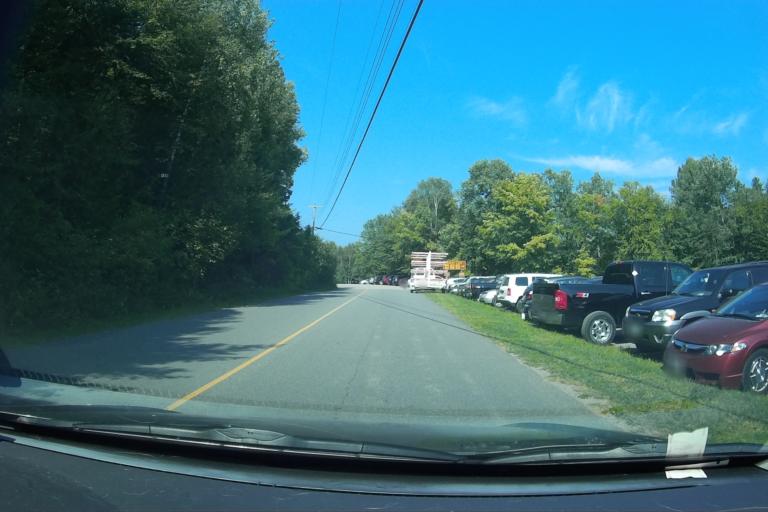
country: CA
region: Ontario
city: Huntsville
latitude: 45.5338
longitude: -78.7061
